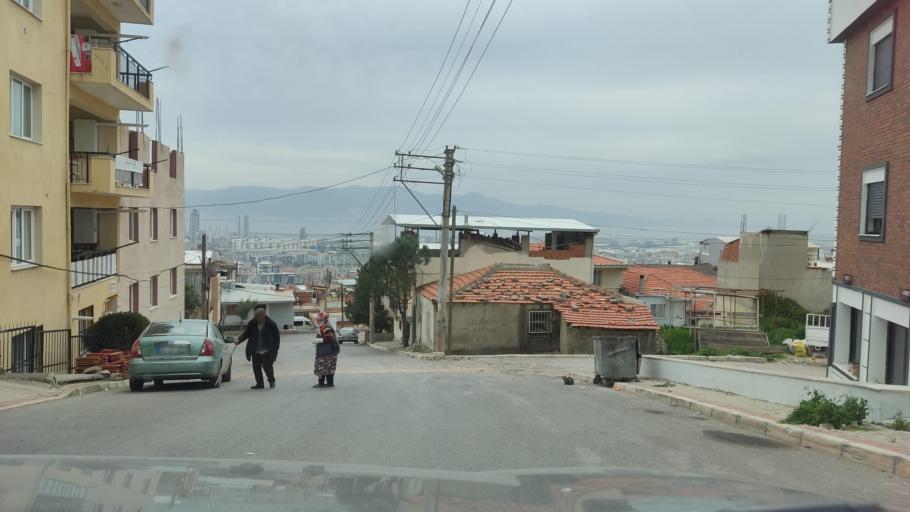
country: TR
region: Izmir
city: Karsiyaka
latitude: 38.4985
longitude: 27.0733
